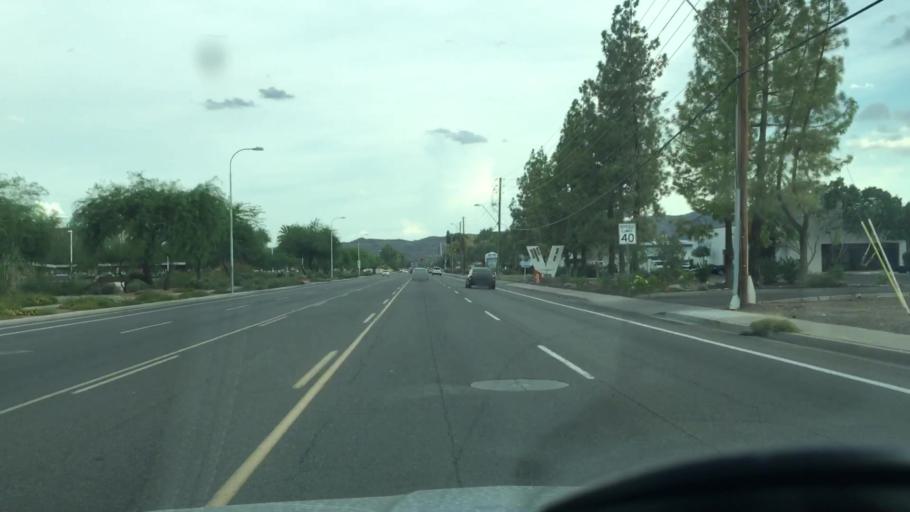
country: US
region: Arizona
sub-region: Maricopa County
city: Guadalupe
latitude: 33.4030
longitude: -111.9954
